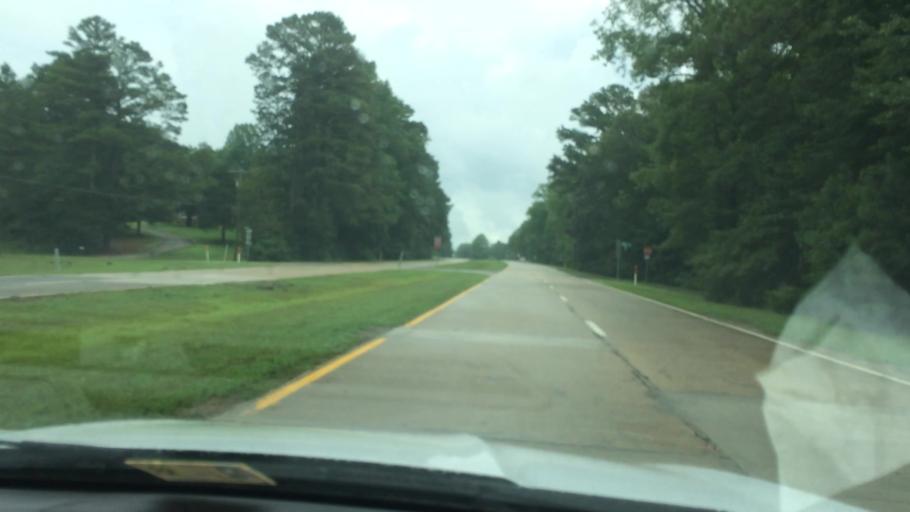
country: US
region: Virginia
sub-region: New Kent County
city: New Kent
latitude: 37.4397
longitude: -77.0285
